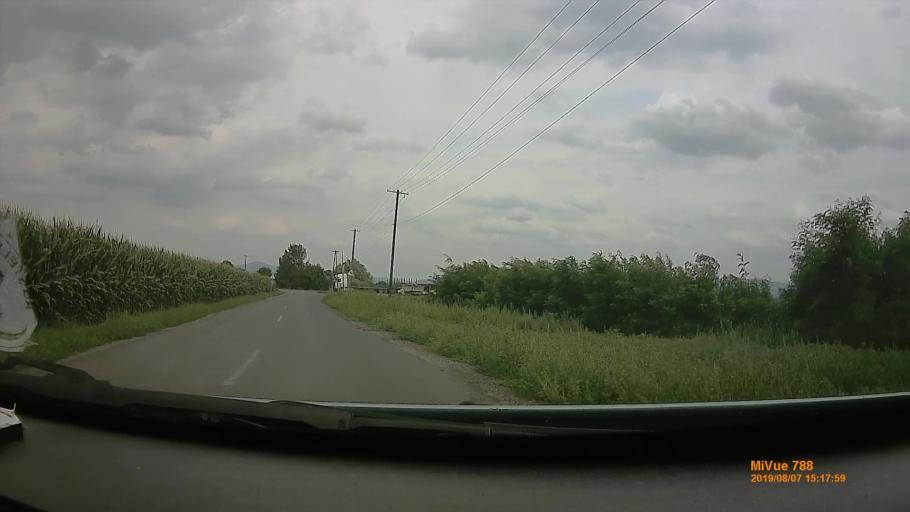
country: HU
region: Borsod-Abauj-Zemplen
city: Encs
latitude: 48.3429
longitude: 21.1364
